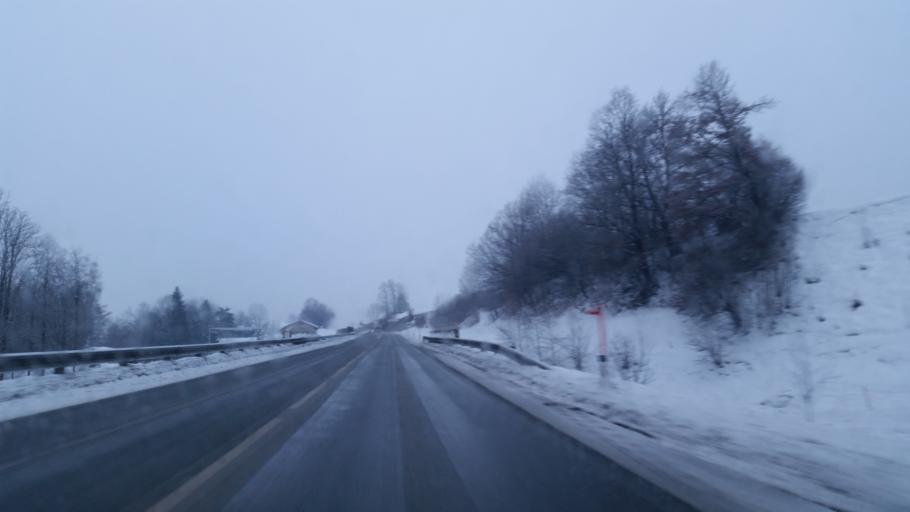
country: AT
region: Tyrol
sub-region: Politischer Bezirk Kufstein
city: Ellmau
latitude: 47.5145
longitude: 12.3367
